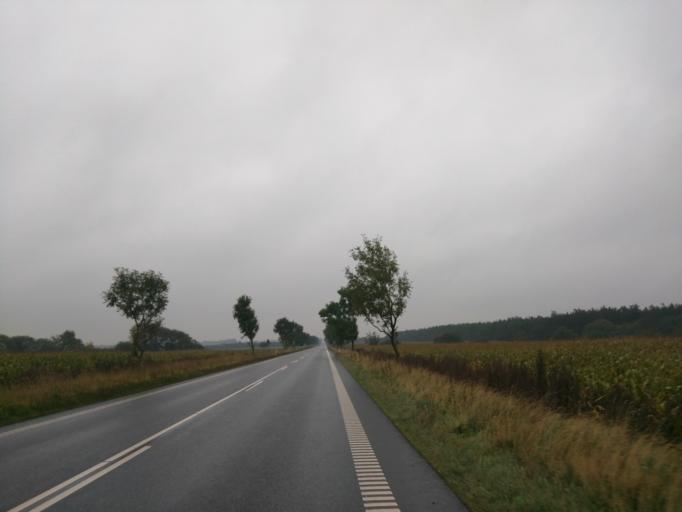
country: DK
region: Central Jutland
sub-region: Viborg Kommune
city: Viborg
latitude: 56.3758
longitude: 9.4413
